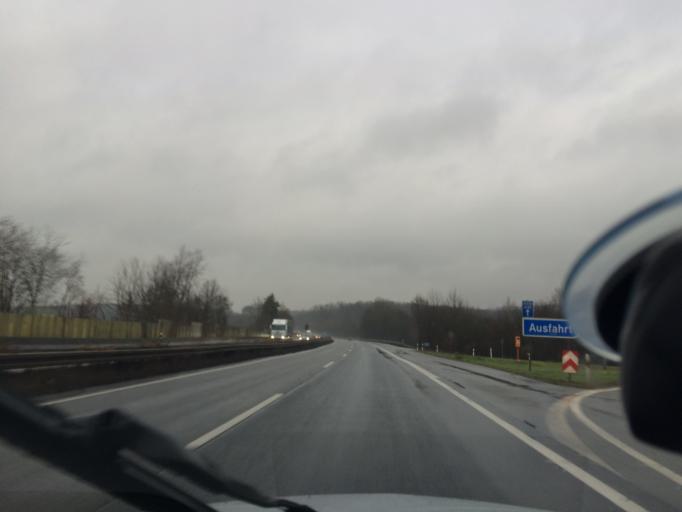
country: DE
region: Hesse
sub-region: Regierungsbezirk Giessen
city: Alten Buseck
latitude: 50.6087
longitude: 8.7179
